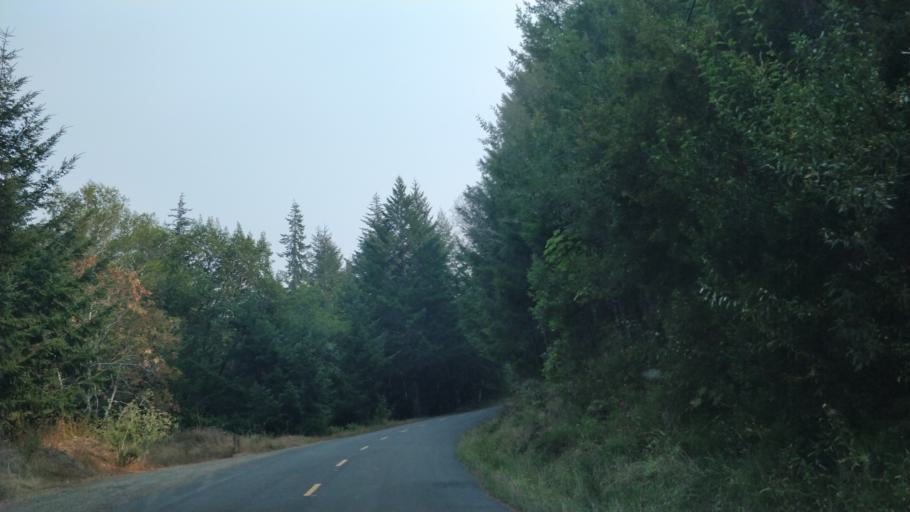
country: US
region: California
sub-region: Humboldt County
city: Rio Dell
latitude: 40.3046
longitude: -124.2574
